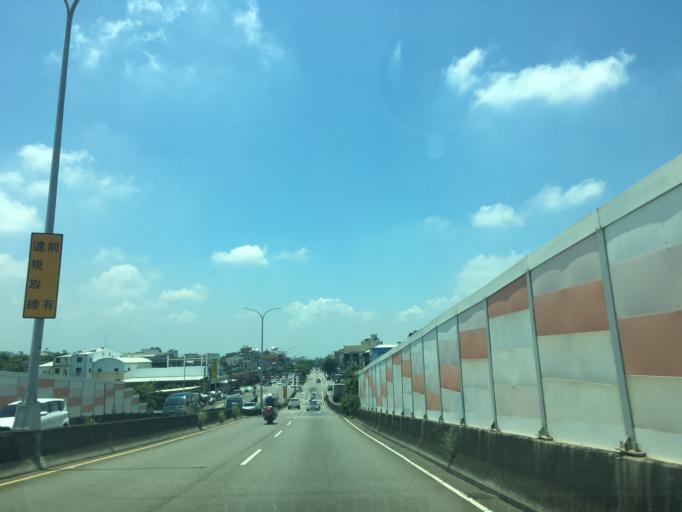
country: TW
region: Taiwan
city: Fengyuan
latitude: 24.2486
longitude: 120.7032
